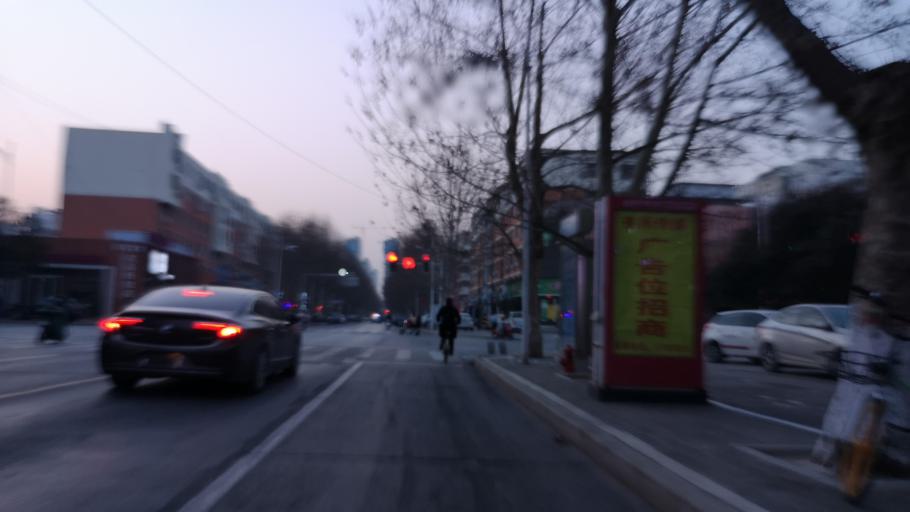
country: CN
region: Henan Sheng
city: Zhongyuanlu
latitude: 35.7664
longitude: 115.0635
